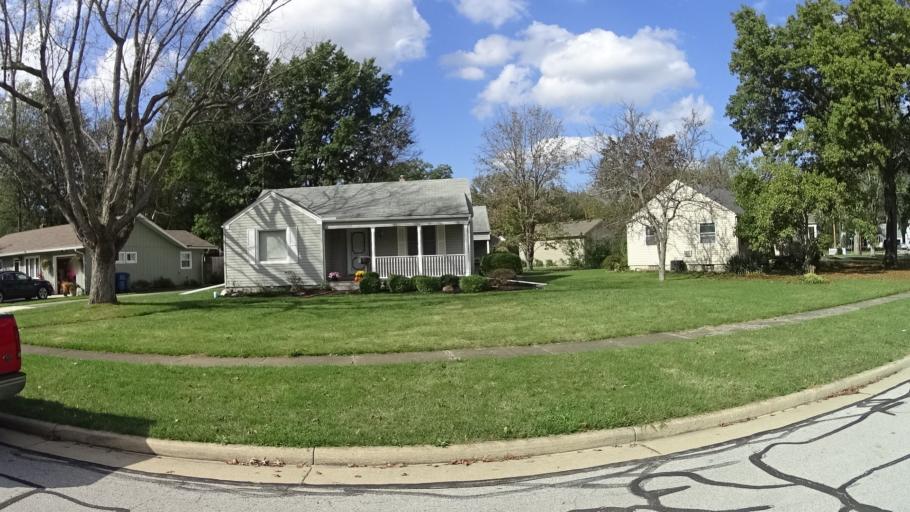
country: US
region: Ohio
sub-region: Lorain County
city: Grafton
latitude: 41.2701
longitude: -82.0474
